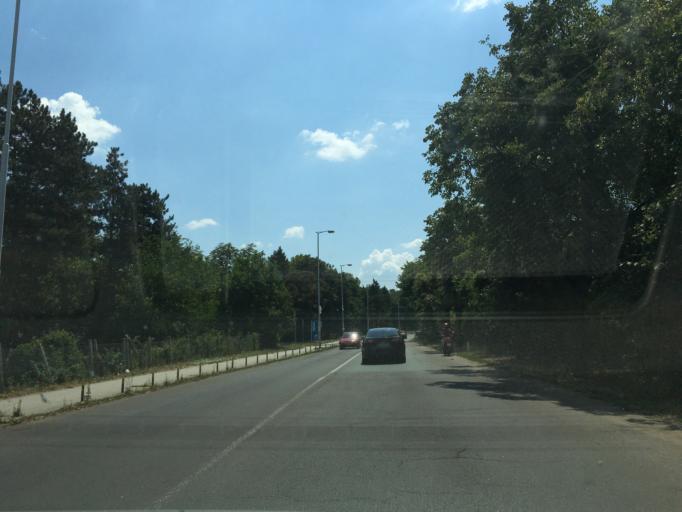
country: RS
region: Central Serbia
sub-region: Belgrade
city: Mladenovac
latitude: 44.4502
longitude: 20.6849
